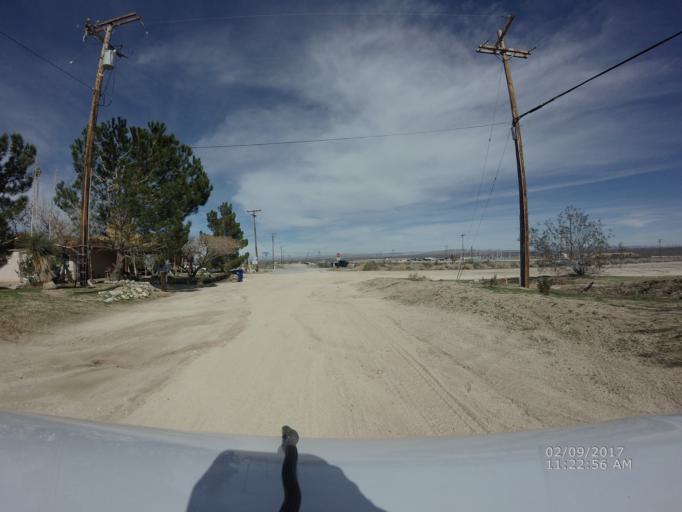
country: US
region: California
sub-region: Los Angeles County
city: Littlerock
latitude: 34.5057
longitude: -117.9229
